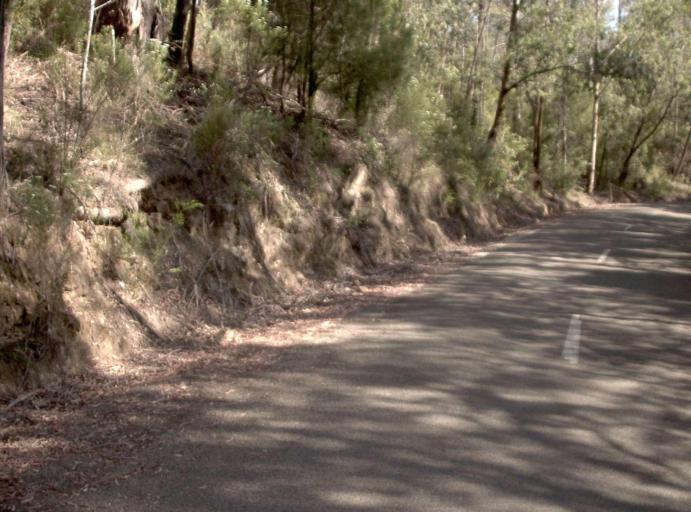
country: AU
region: Victoria
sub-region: East Gippsland
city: Lakes Entrance
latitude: -37.4799
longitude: 148.5561
